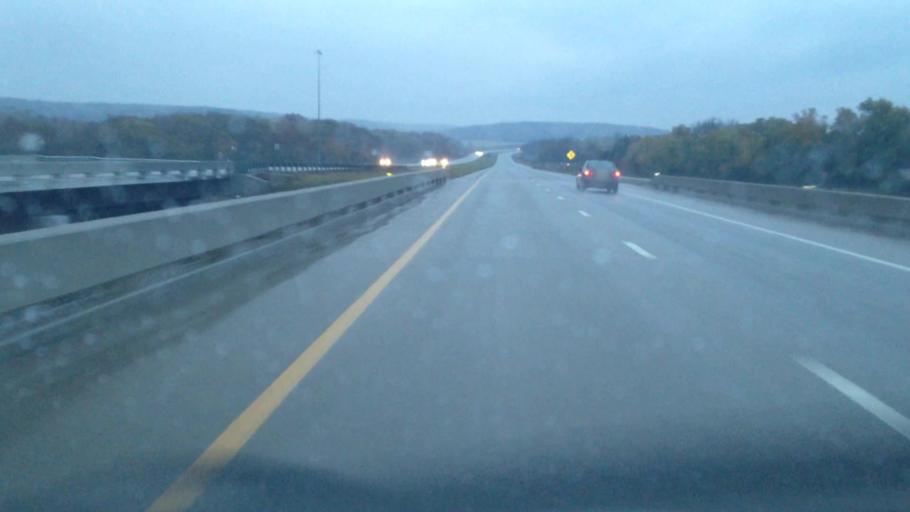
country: US
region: Kansas
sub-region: Douglas County
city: Lawrence
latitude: 38.8846
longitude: -95.2585
